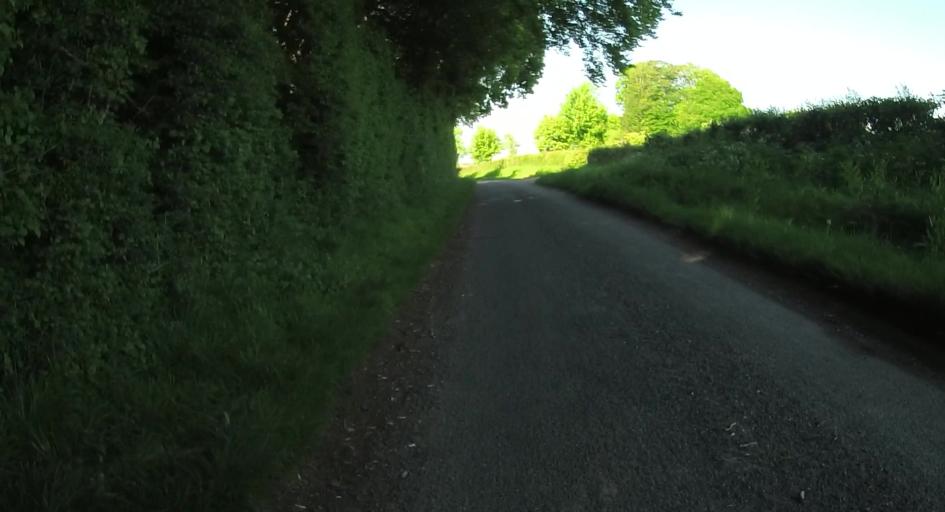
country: GB
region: England
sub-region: Hampshire
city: Overton
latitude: 51.1614
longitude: -1.2218
